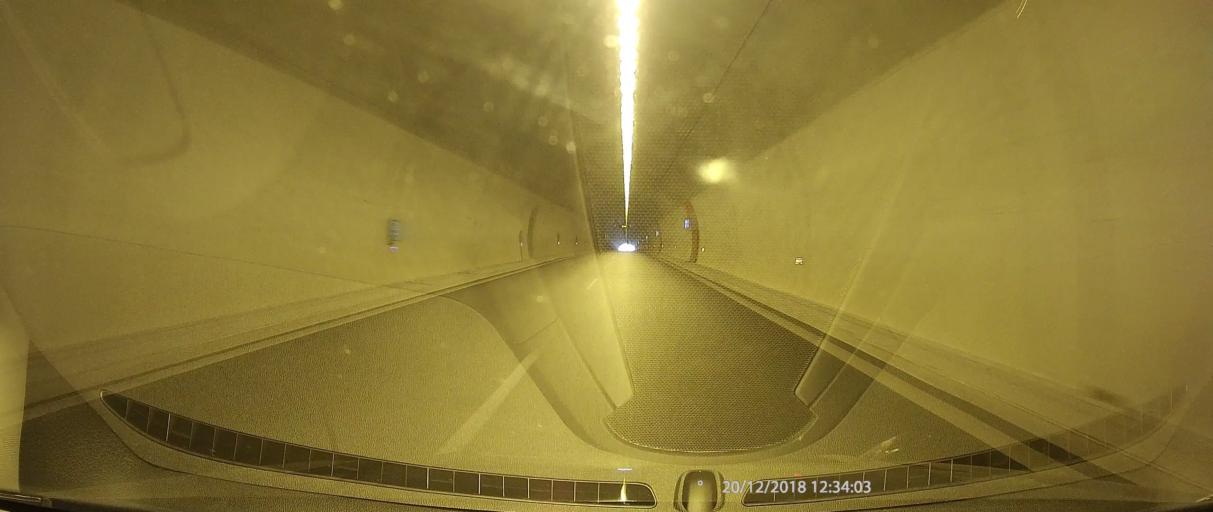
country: GR
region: West Greece
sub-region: Nomos Aitolias kai Akarnanias
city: Antirrio
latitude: 38.3531
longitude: 21.7254
